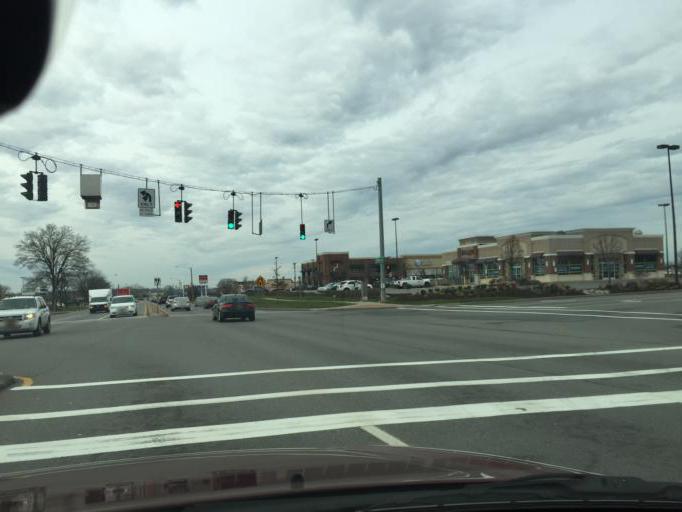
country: US
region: New York
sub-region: Monroe County
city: Rochester
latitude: 43.0872
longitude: -77.6244
